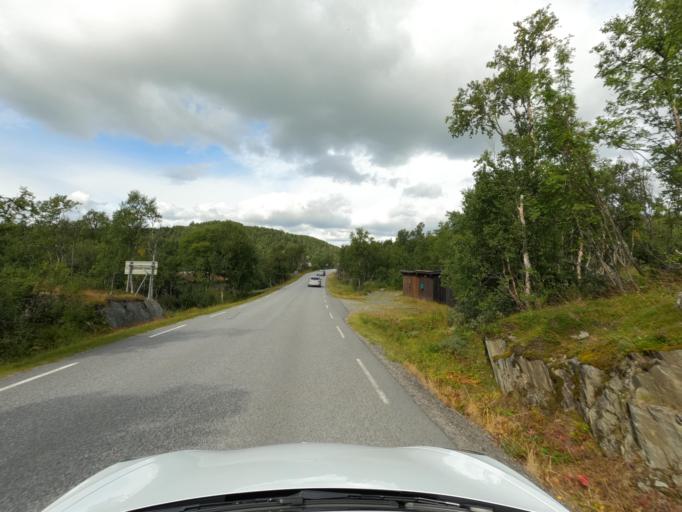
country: NO
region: Telemark
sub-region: Tinn
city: Rjukan
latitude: 59.8202
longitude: 8.3191
